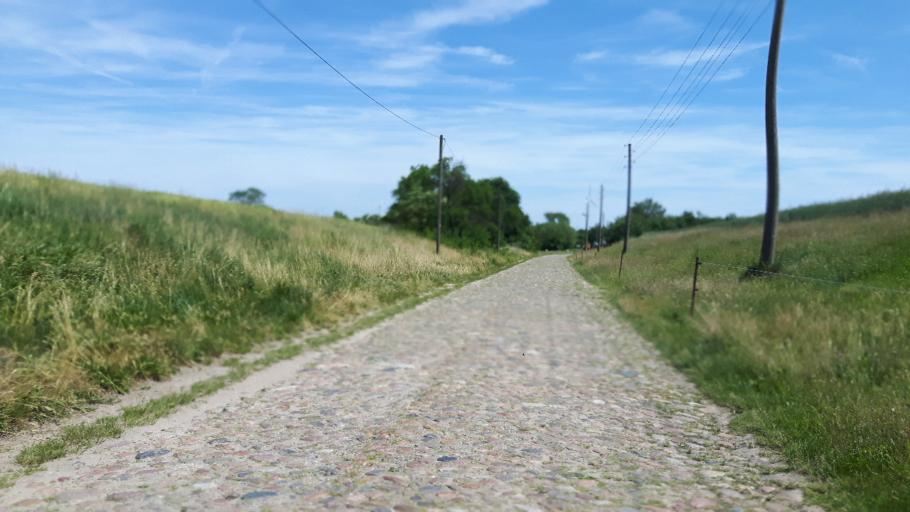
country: DE
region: Saxony-Anhalt
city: Kropstadt
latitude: 52.0066
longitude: 12.7262
